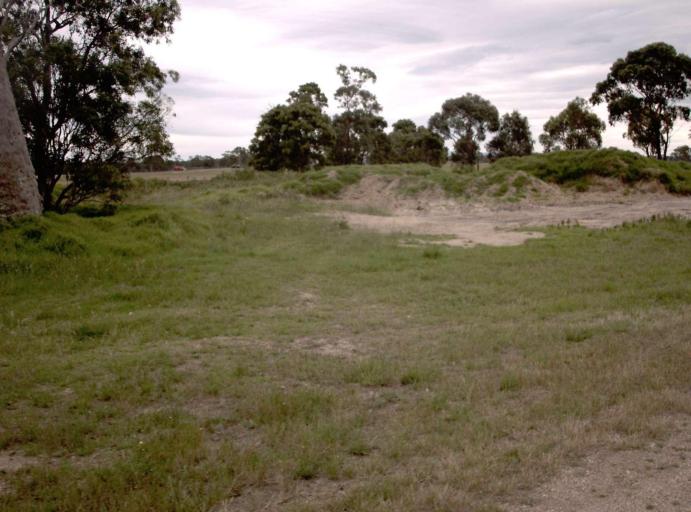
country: AU
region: Victoria
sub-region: East Gippsland
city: Bairnsdale
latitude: -37.9344
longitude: 147.5316
